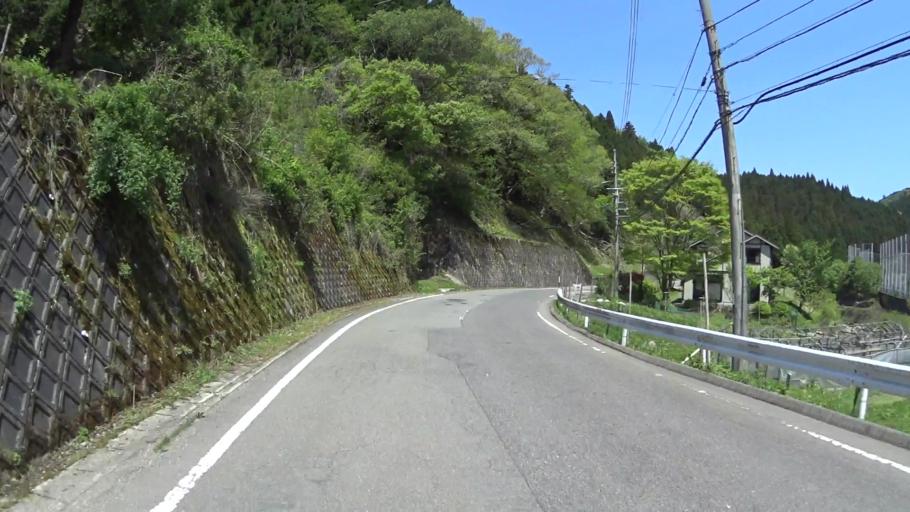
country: JP
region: Shiga Prefecture
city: Kitahama
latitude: 35.1770
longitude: 135.7848
